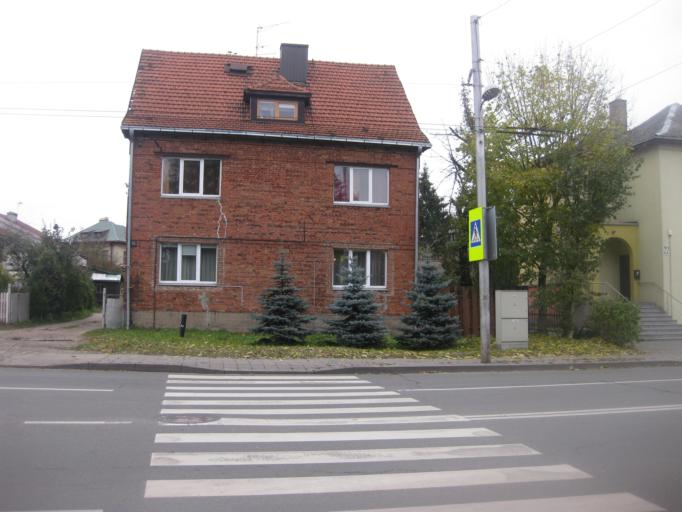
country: LT
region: Kauno apskritis
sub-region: Kaunas
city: Eiguliai
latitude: 54.9116
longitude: 23.9249
